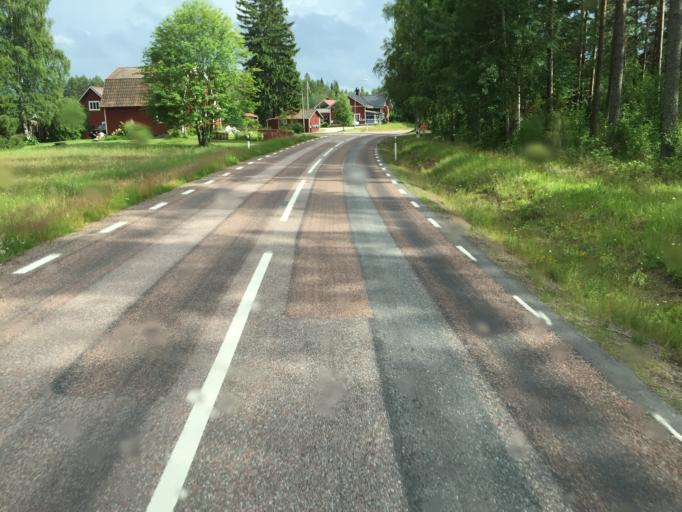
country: SE
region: Dalarna
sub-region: Vansbro Kommun
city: Jarna
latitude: 60.5256
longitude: 14.4464
